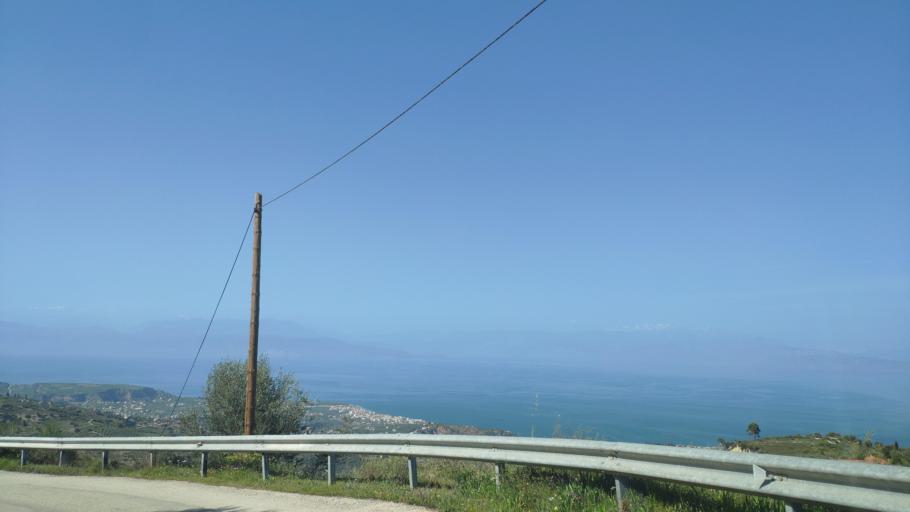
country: GR
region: West Greece
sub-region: Nomos Achaias
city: Aiyira
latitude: 38.1182
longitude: 22.3344
